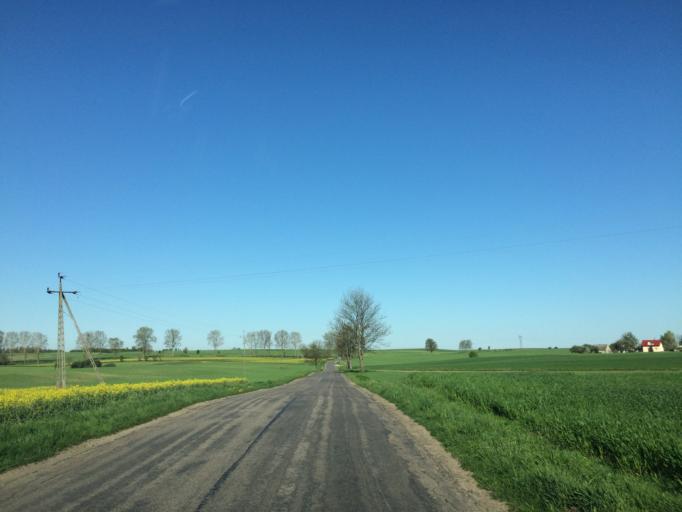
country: PL
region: Warmian-Masurian Voivodeship
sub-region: Powiat dzialdowski
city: Rybno
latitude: 53.3963
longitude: 19.8851
